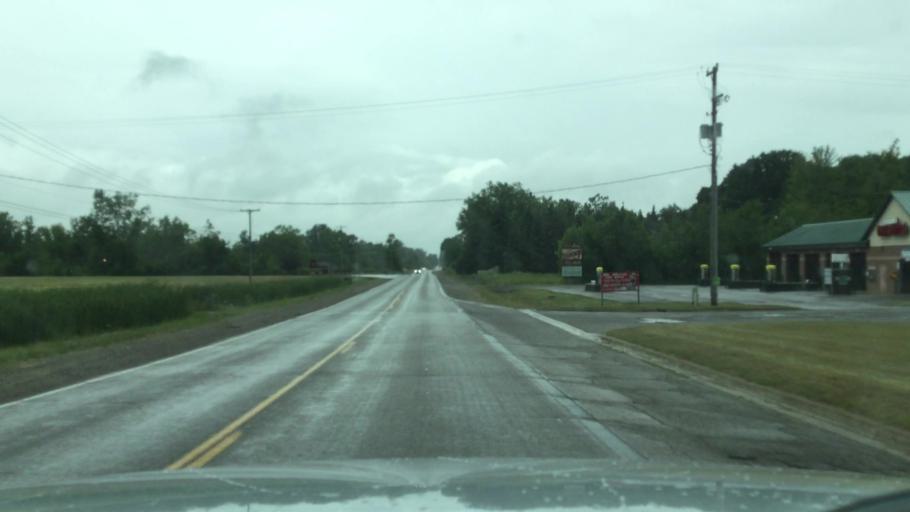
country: US
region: Michigan
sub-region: Genesee County
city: Clio
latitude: 43.1189
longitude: -83.7662
